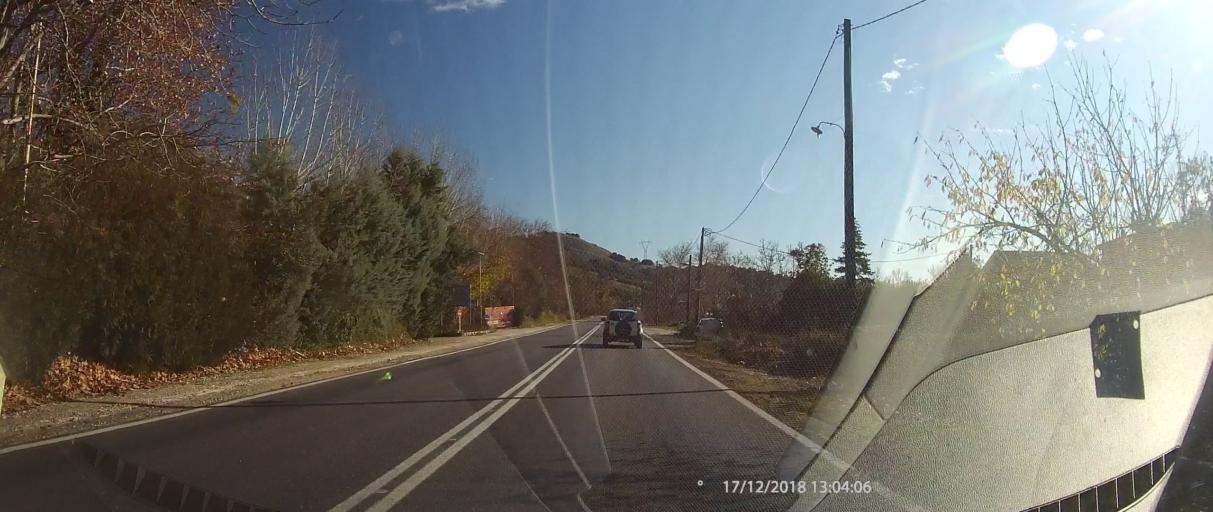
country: GR
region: Thessaly
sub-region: Trikala
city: Kastraki
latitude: 39.7089
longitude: 21.6087
